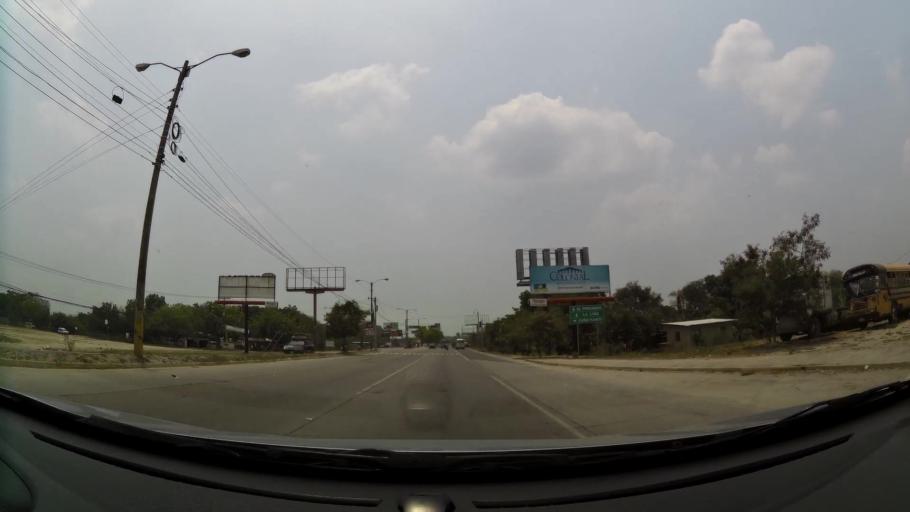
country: HN
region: Cortes
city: La Lima
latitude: 15.4560
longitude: -87.9511
